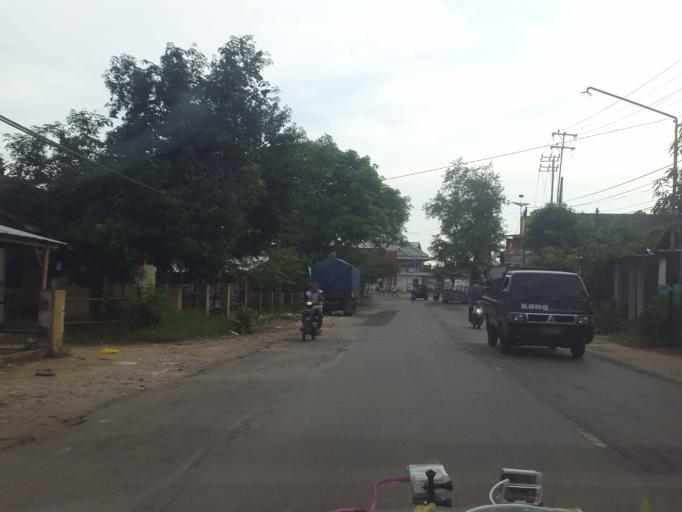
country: ID
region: East Java
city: Senmasen
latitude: -6.9973
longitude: 113.8666
